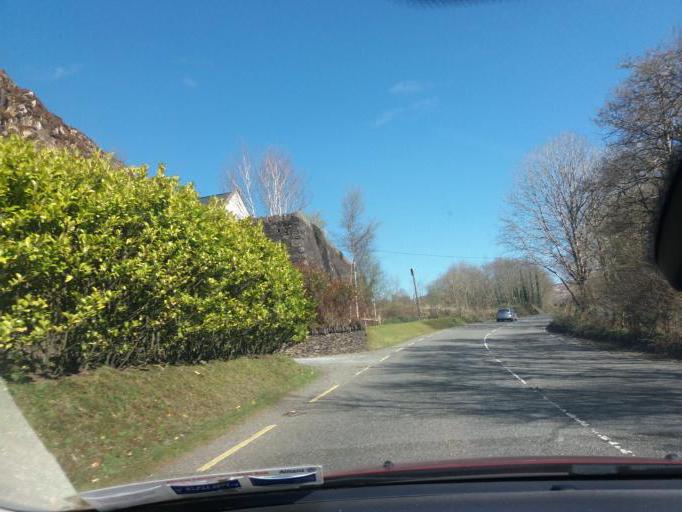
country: IE
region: Munster
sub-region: Ciarrai
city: Cill Airne
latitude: 51.9254
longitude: -9.3844
